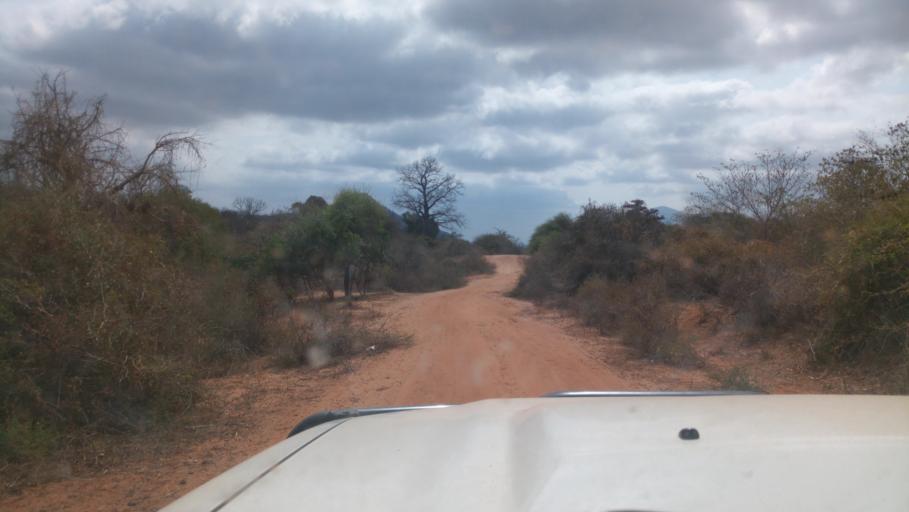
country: KE
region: Kitui
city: Kitui
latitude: -1.8366
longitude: 38.3030
